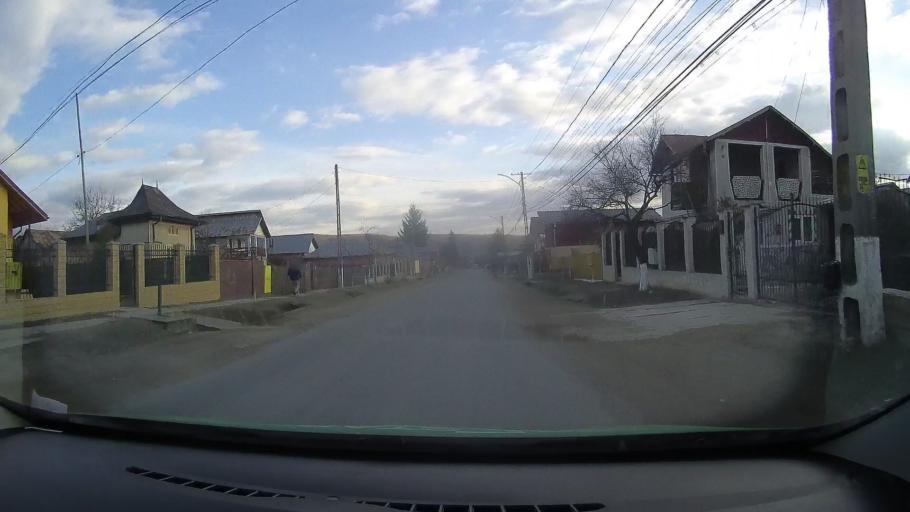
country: RO
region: Dambovita
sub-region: Comuna Ocnita
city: Ocnita
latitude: 44.9859
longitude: 25.5541
